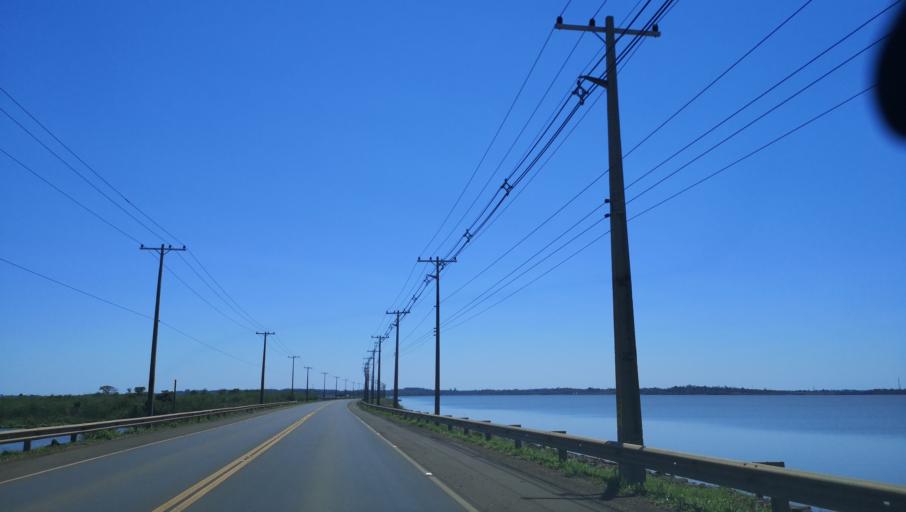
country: PY
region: Itapua
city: Carmen del Parana
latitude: -27.2123
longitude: -56.1560
